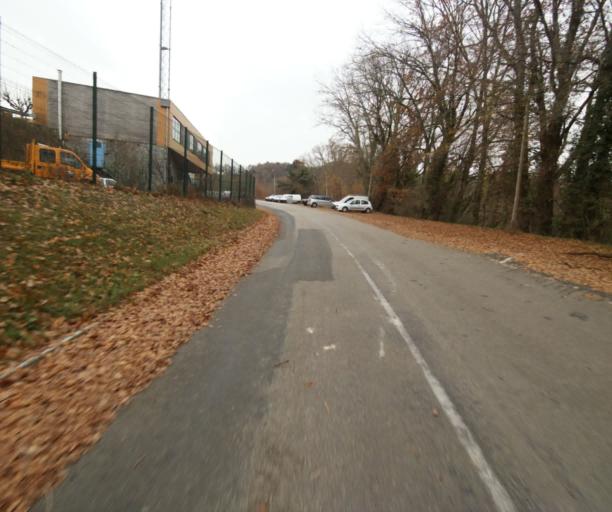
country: FR
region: Limousin
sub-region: Departement de la Correze
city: Tulle
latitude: 45.2713
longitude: 1.7361
